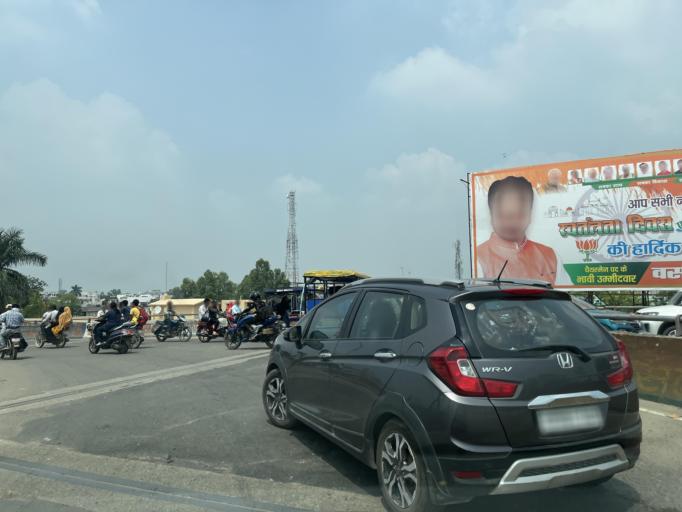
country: IN
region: Uttar Pradesh
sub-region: Bijnor
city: Najibabad
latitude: 29.6055
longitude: 78.3433
